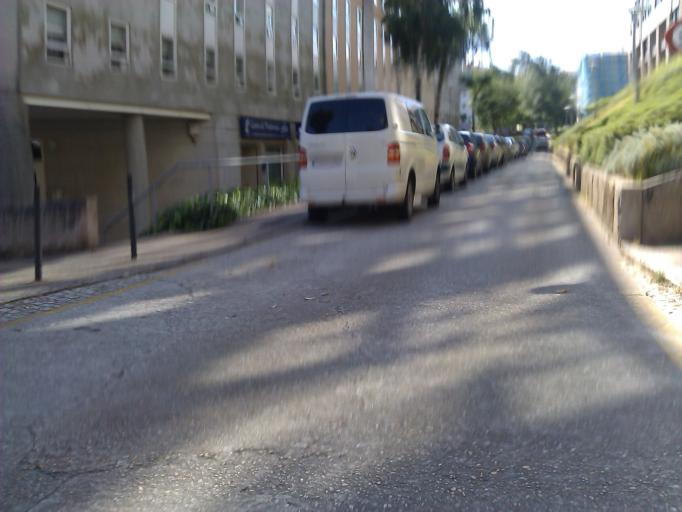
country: ES
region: Galicia
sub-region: Provincia da Coruna
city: Santiago de Compostela
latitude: 42.8818
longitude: -8.5284
